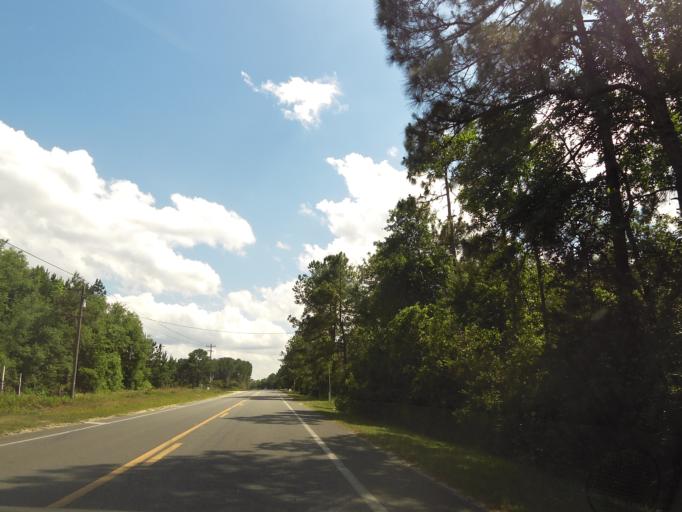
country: US
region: Florida
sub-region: Clay County
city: Keystone Heights
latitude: 29.8429
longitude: -81.9207
